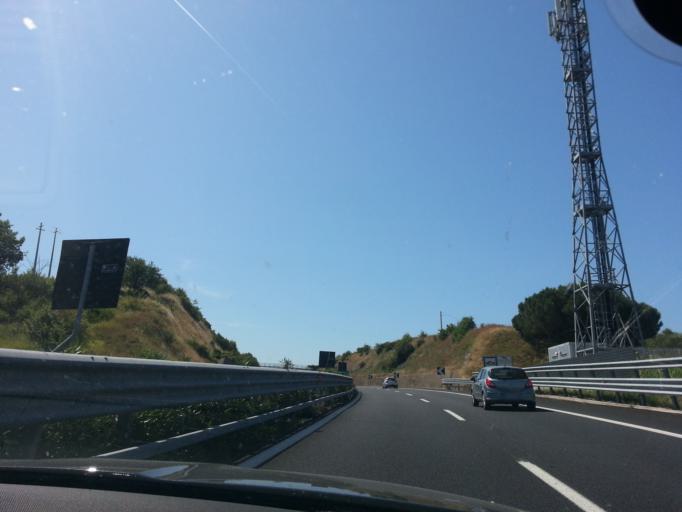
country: IT
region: Latium
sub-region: Citta metropolitana di Roma Capitale
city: Civitavecchia
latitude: 42.1184
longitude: 11.8227
